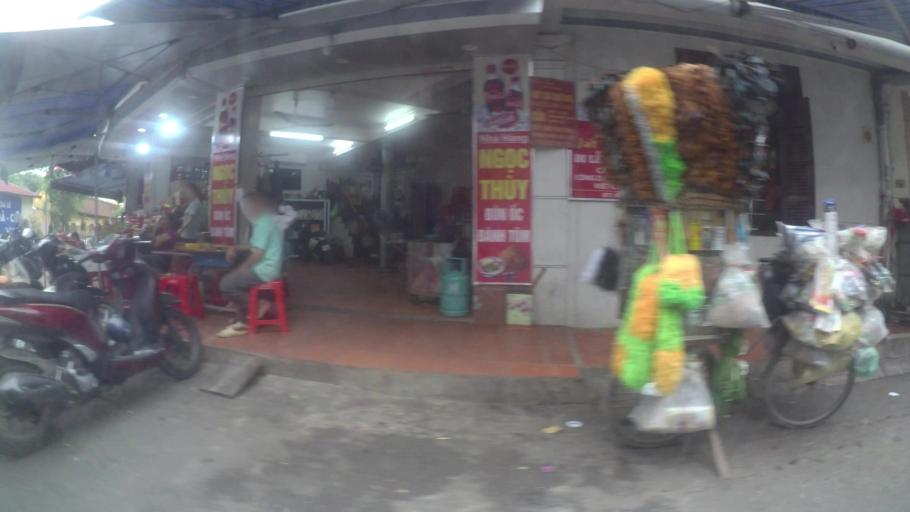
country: VN
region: Ha Noi
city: Tay Ho
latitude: 21.0553
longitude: 105.8199
